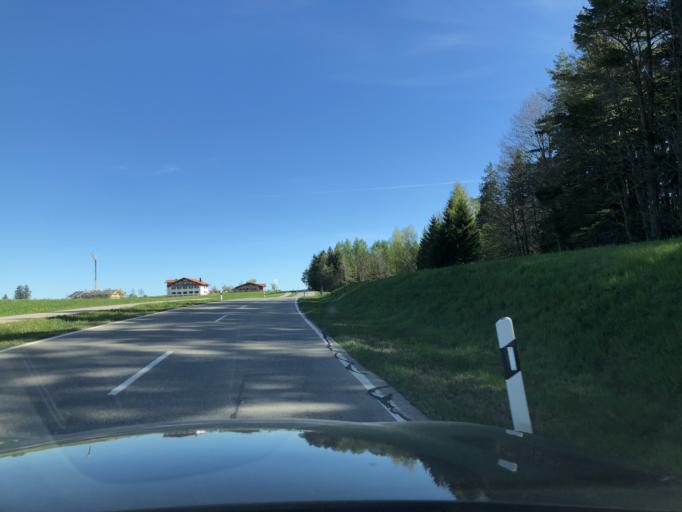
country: DE
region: Bavaria
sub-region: Swabia
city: Wald
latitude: 47.7123
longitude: 10.5542
